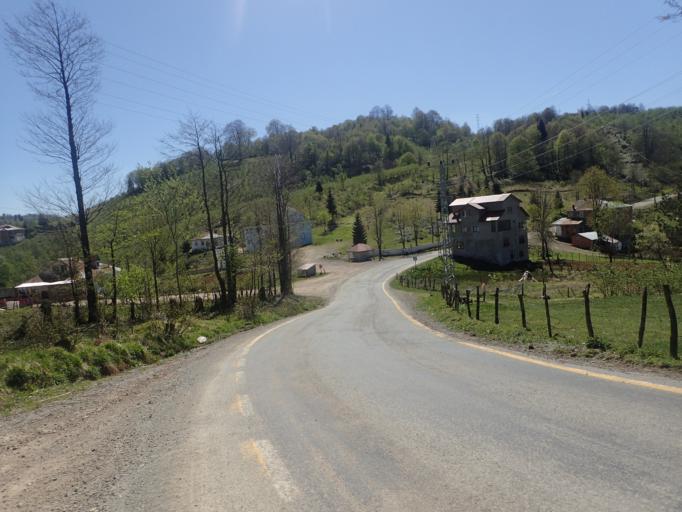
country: TR
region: Ordu
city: Kabaduz
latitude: 40.7976
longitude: 37.9150
